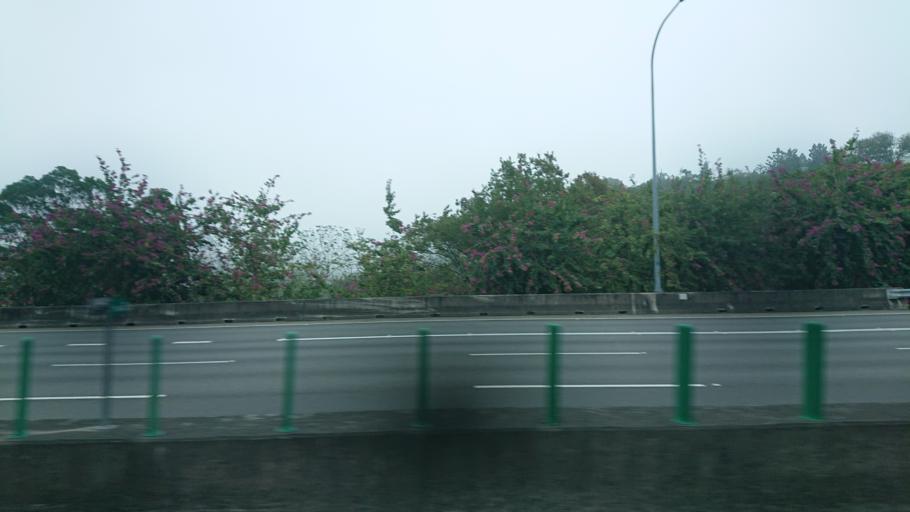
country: TW
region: Taiwan
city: Fengyuan
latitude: 24.3314
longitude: 120.7161
